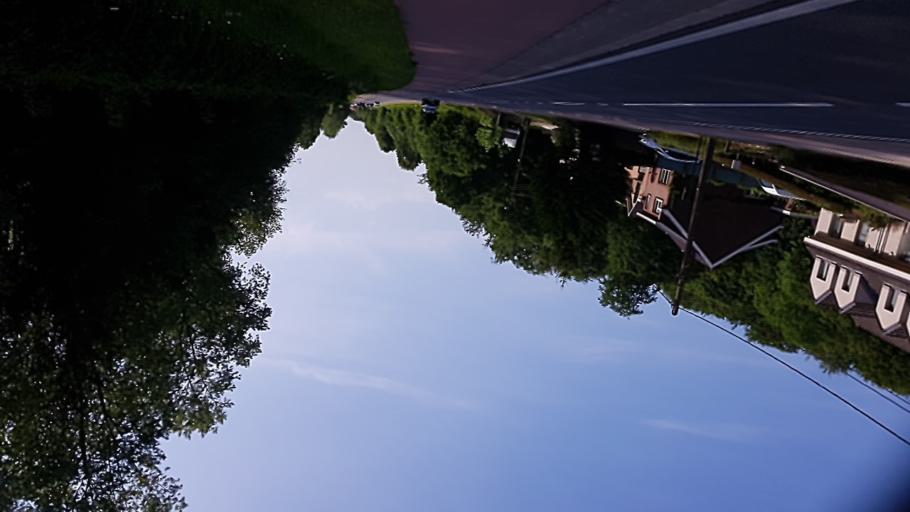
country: BE
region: Flanders
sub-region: Provincie Vlaams-Brabant
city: Huldenberg
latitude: 50.7861
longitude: 4.5690
